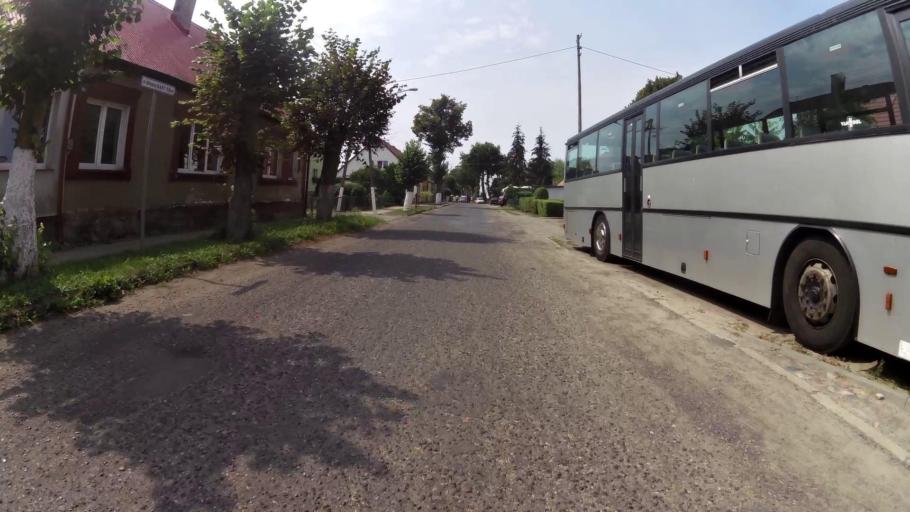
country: PL
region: West Pomeranian Voivodeship
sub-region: Powiat gryfinski
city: Moryn
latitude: 52.8699
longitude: 14.4721
